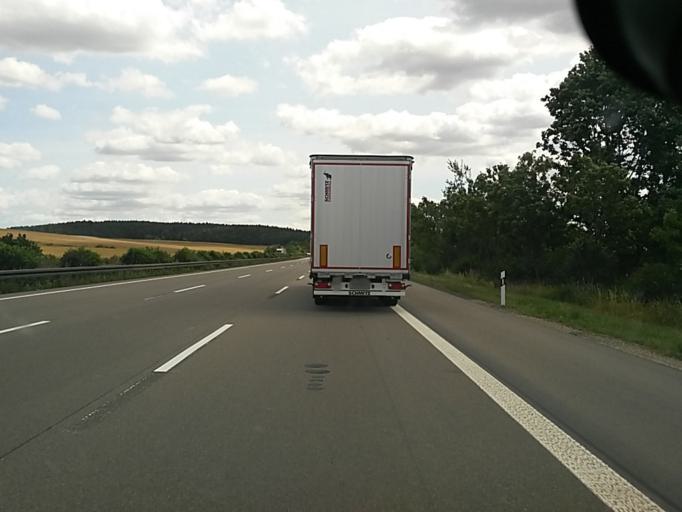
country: DE
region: Thuringia
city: Ruttersdorf-Lotschen
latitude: 50.8743
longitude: 11.7166
